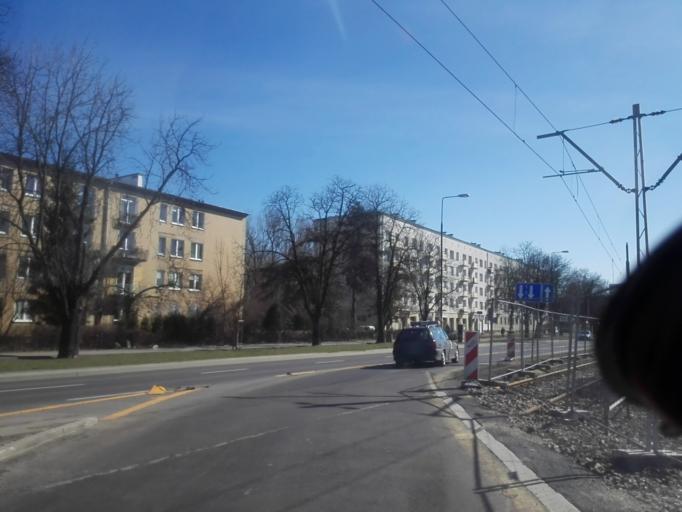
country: PL
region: Masovian Voivodeship
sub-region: Warszawa
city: Ochota
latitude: 52.1979
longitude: 21.0014
